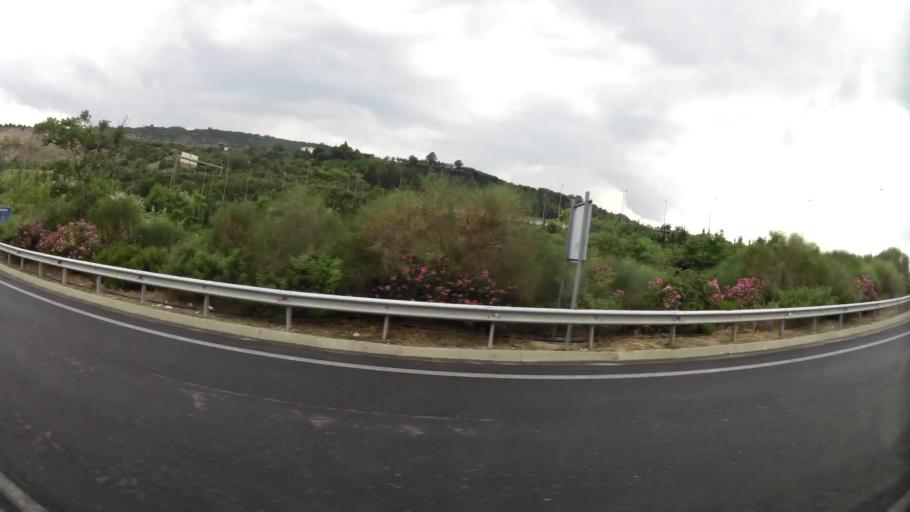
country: GR
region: Central Macedonia
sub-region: Nomos Imathias
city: Veroia
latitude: 40.5057
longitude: 22.2310
